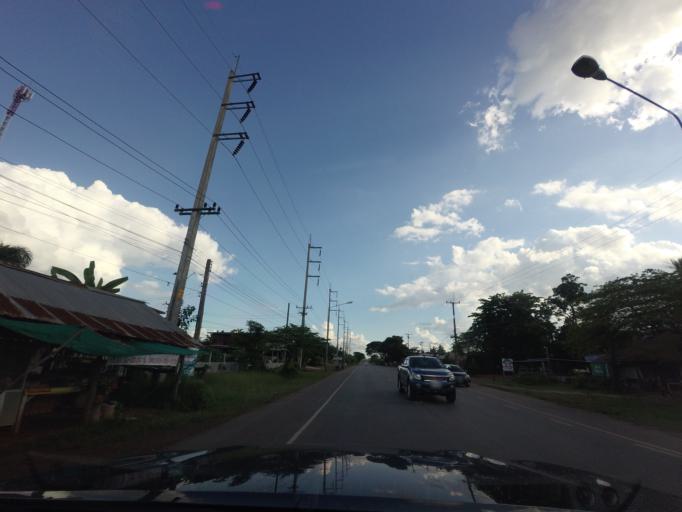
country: TH
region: Changwat Udon Thani
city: Thung Fon
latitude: 17.5084
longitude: 103.2034
